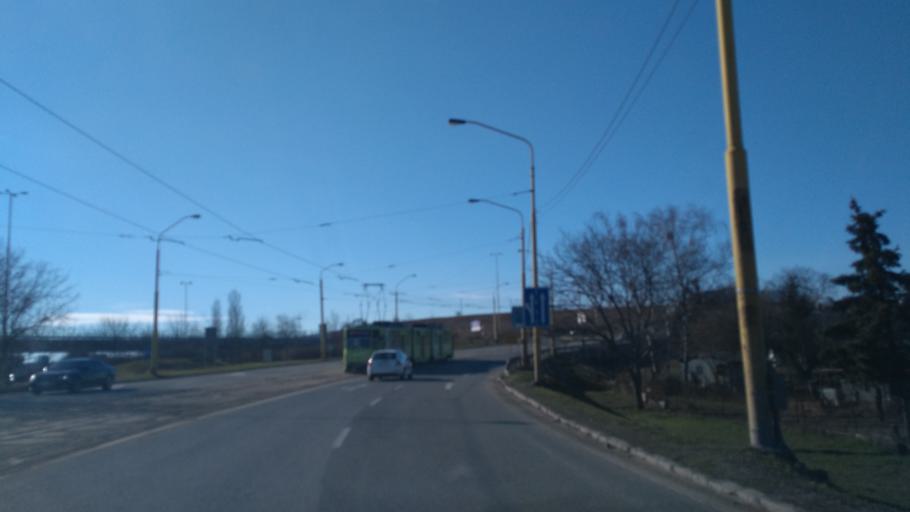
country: SK
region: Kosicky
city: Kosice
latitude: 48.6884
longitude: 21.2597
